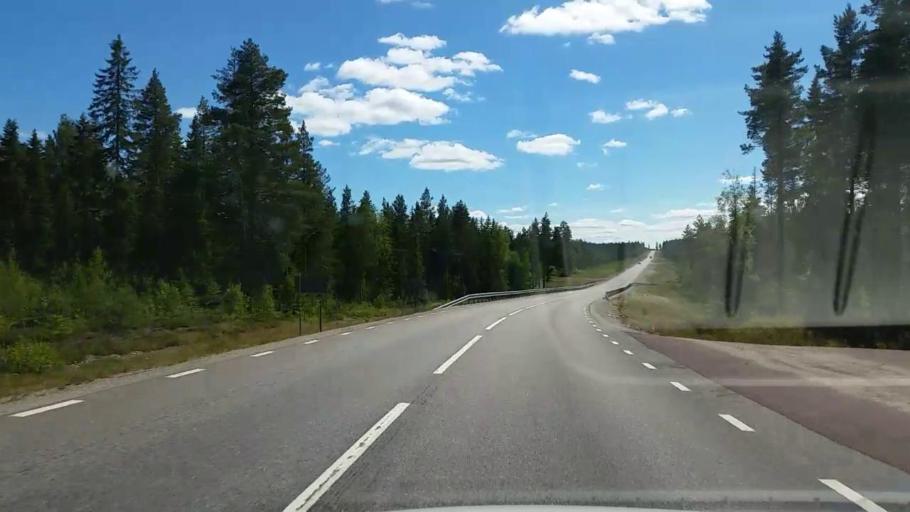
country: SE
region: Gaevleborg
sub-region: Bollnas Kommun
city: Vittsjo
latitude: 61.1224
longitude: 15.8664
